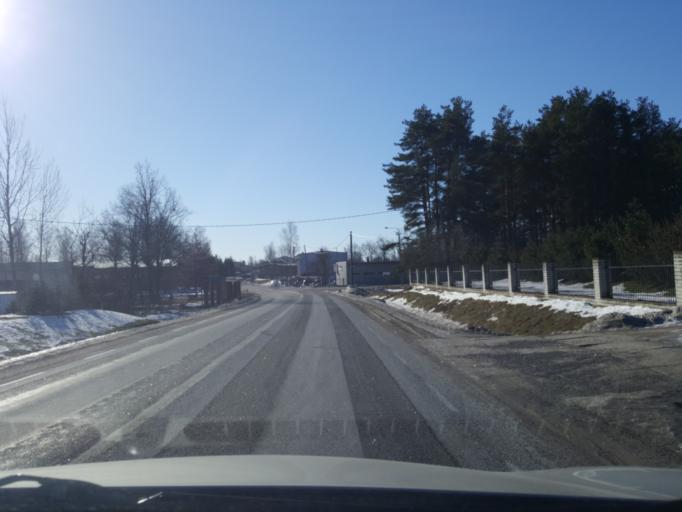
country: EE
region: Viljandimaa
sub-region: Viljandi linn
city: Viljandi
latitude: 58.3795
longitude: 25.6028
